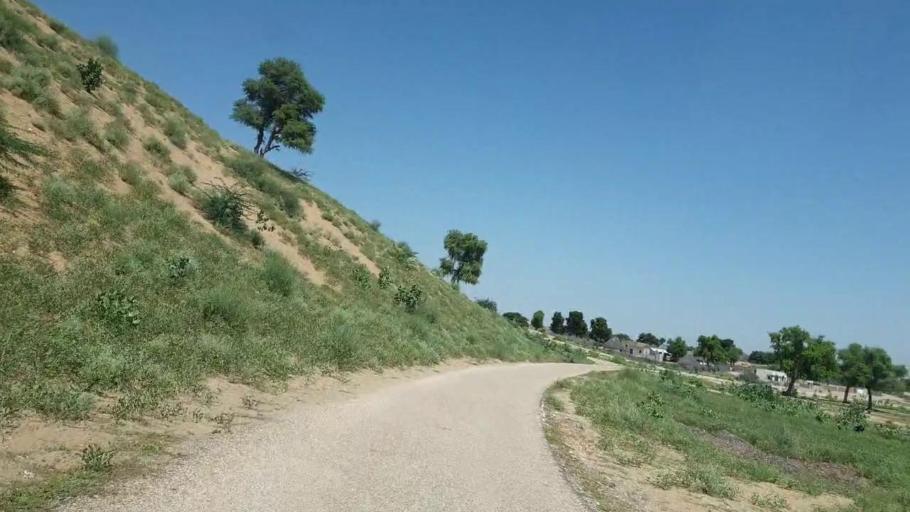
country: PK
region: Sindh
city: Islamkot
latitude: 25.1560
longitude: 70.4093
